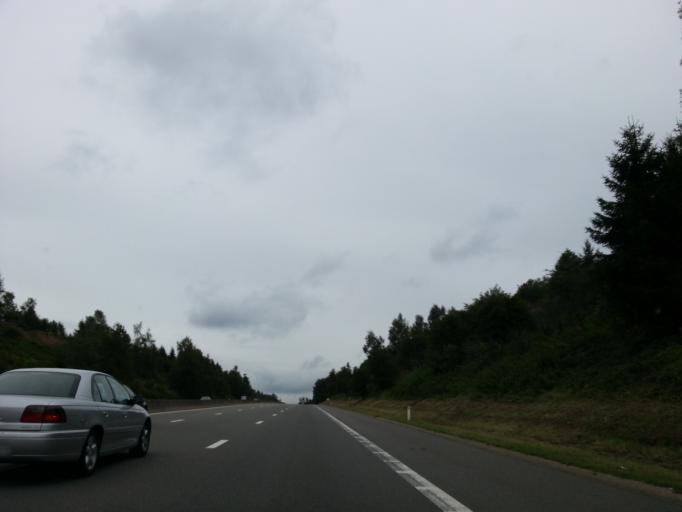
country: BE
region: Wallonia
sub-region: Province de Liege
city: Malmedy
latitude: 50.4304
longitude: 6.0074
